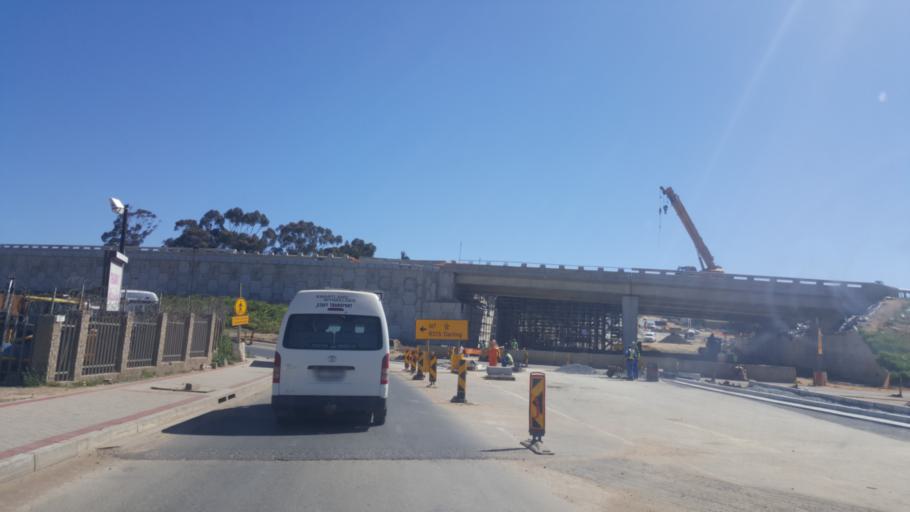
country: ZA
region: Western Cape
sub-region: West Coast District Municipality
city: Malmesbury
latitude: -33.4658
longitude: 18.7185
